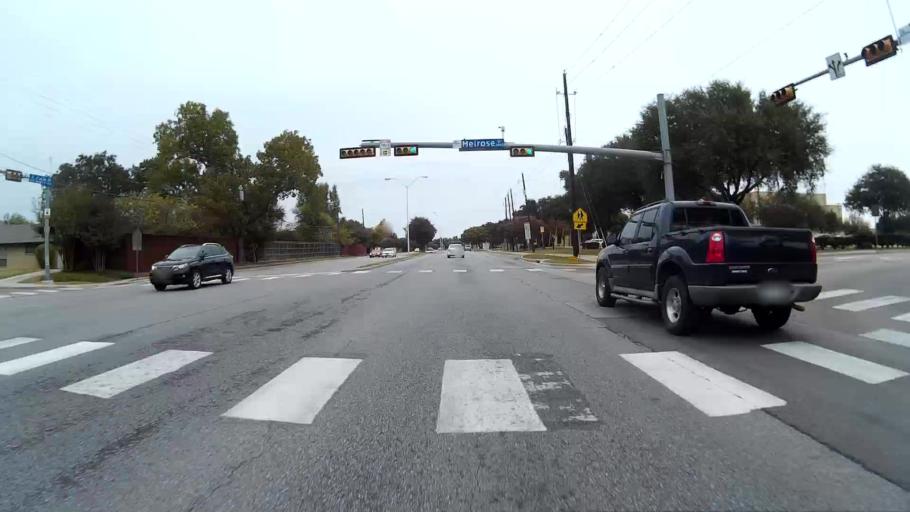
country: US
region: Texas
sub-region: Dallas County
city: Richardson
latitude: 32.9707
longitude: -96.7688
